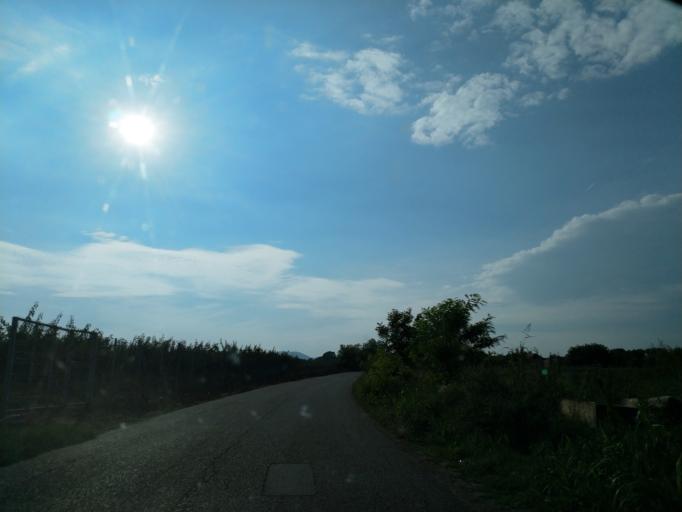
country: RS
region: Central Serbia
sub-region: Pomoravski Okrug
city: Jagodina
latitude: 43.9788
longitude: 21.2309
